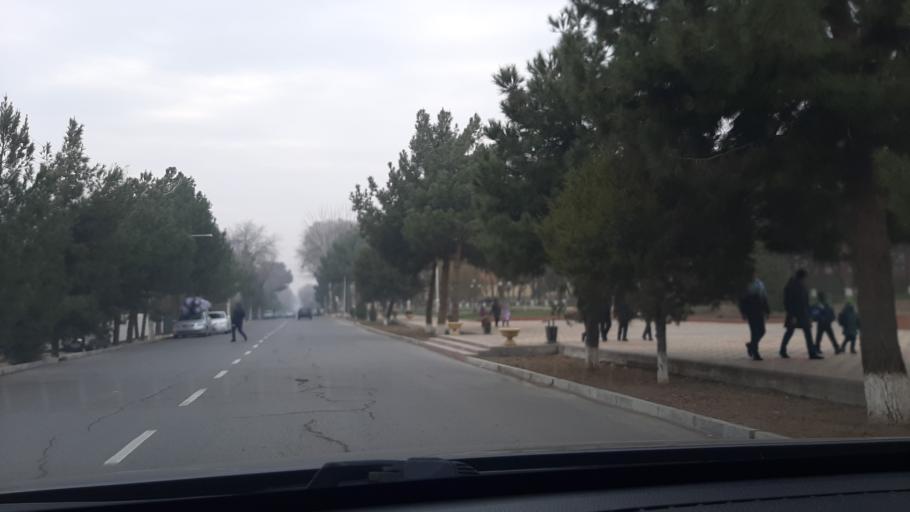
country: TJ
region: Viloyati Sughd
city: Palos
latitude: 40.2674
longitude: 69.8025
